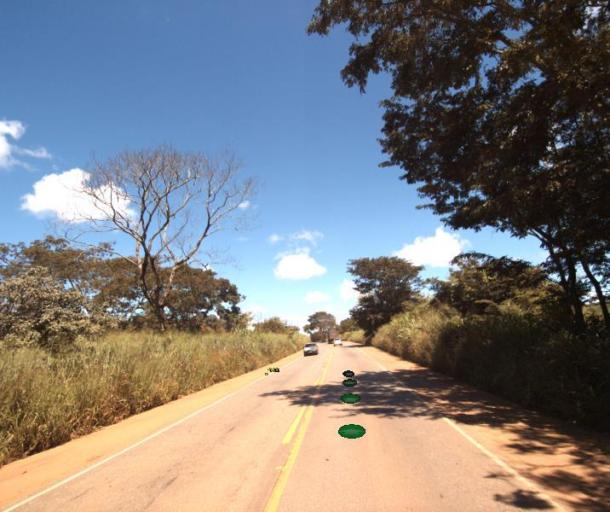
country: BR
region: Goias
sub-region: Anapolis
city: Anapolis
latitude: -16.1223
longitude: -49.0400
